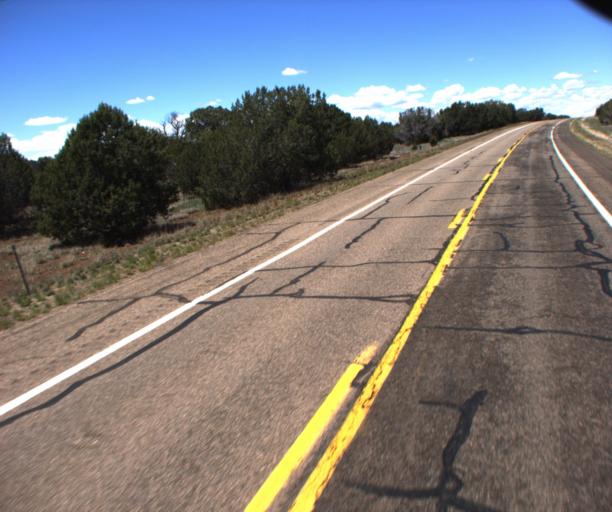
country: US
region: Arizona
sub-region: Yavapai County
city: Paulden
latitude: 35.1616
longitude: -112.4566
